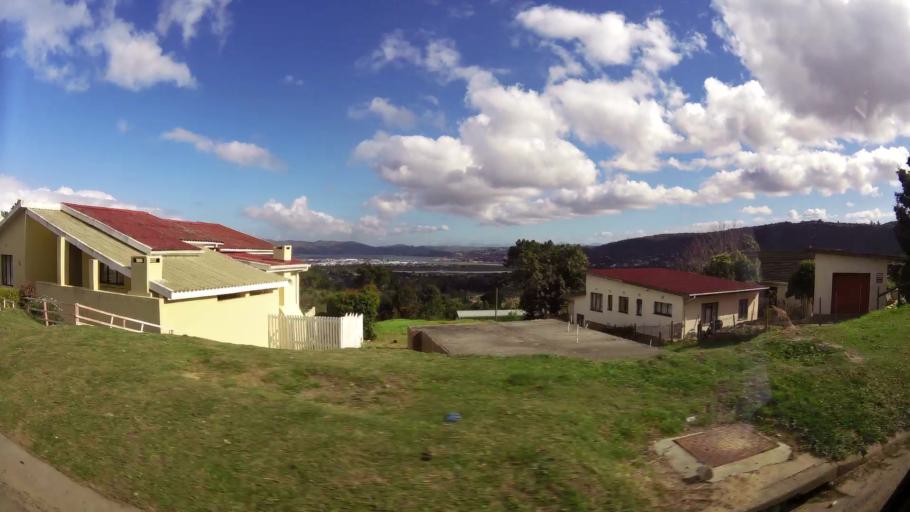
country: ZA
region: Western Cape
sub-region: Eden District Municipality
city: Knysna
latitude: -34.0496
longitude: 23.0826
